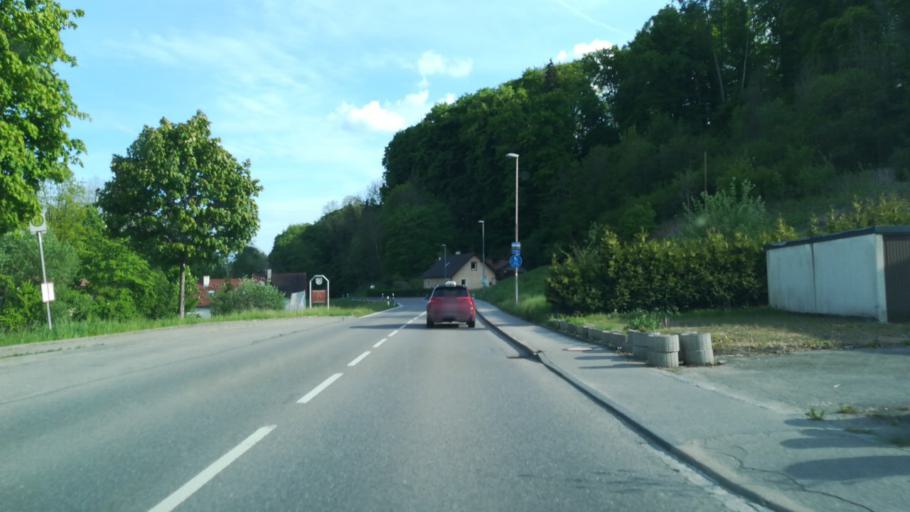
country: DE
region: Baden-Wuerttemberg
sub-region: Freiburg Region
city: Stockach
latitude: 47.8706
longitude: 9.0029
